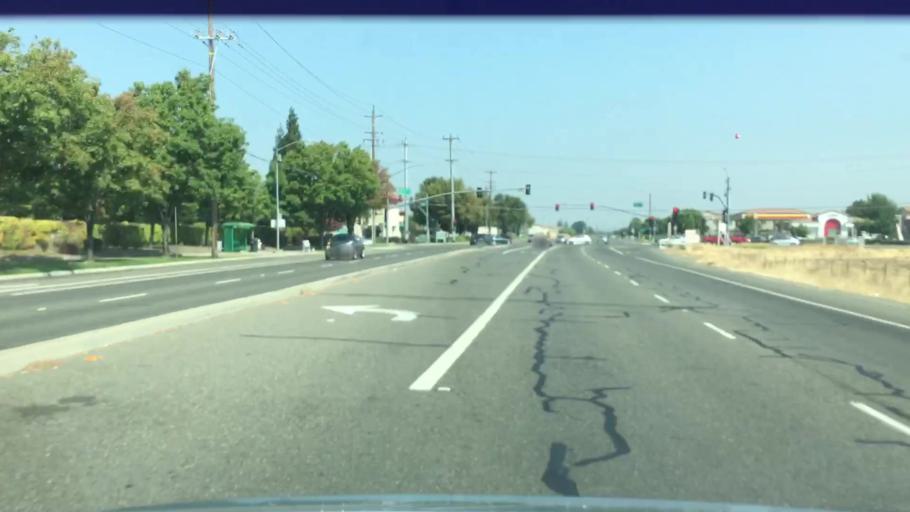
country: US
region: California
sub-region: Sacramento County
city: Laguna
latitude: 38.4368
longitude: -121.4177
